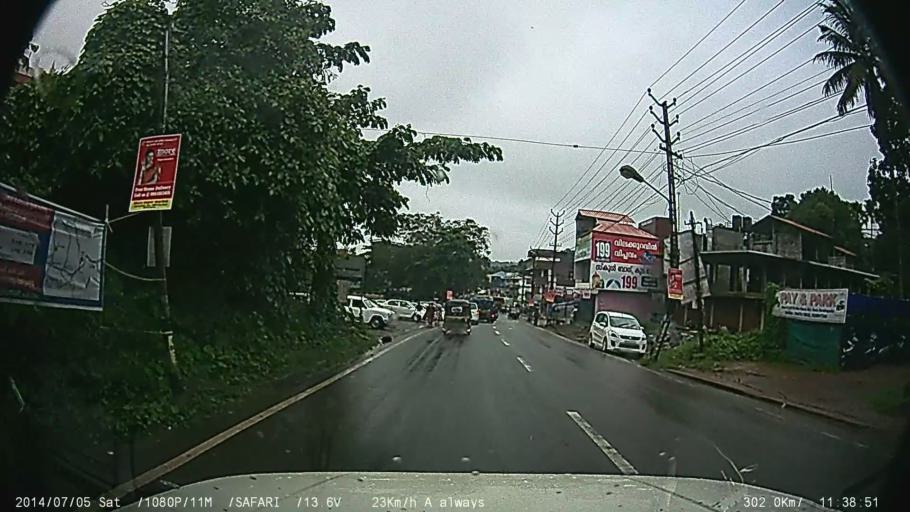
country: IN
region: Kerala
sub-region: Ernakulam
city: Muvattupuzha
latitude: 9.9792
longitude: 76.5793
